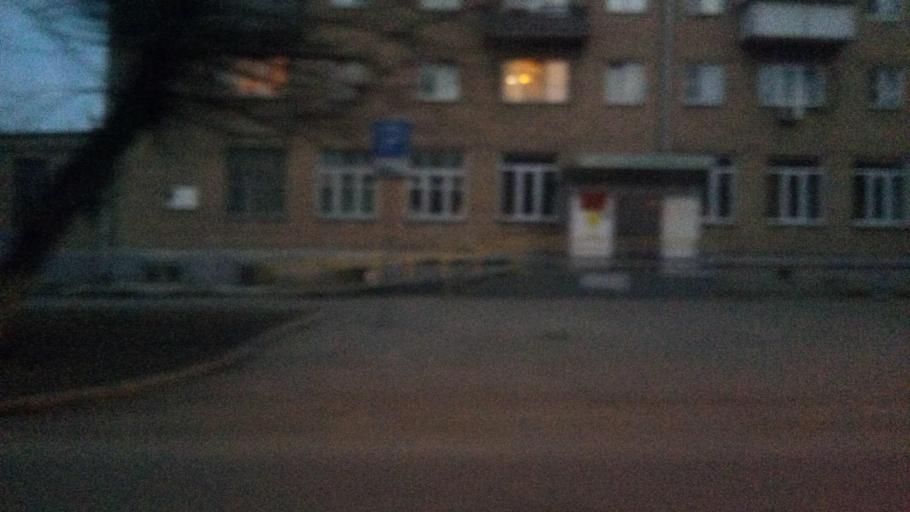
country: RU
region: Chelyabinsk
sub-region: Gorod Chelyabinsk
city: Chelyabinsk
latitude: 55.1679
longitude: 61.4605
